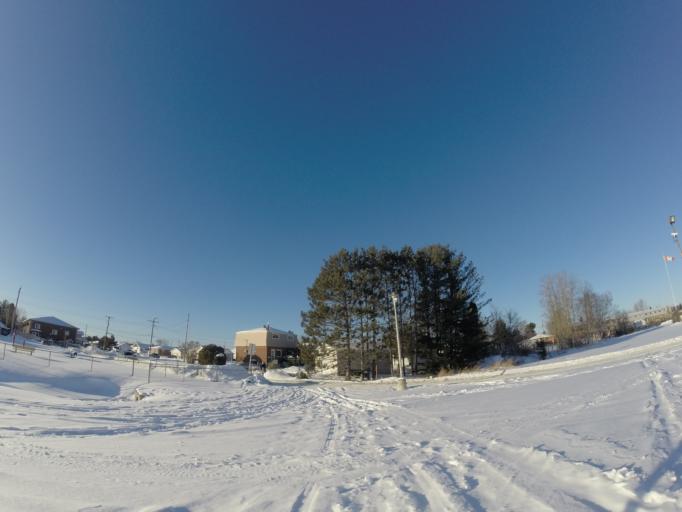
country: CA
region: Ontario
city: Rayside-Balfour
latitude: 46.5758
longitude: -81.1946
